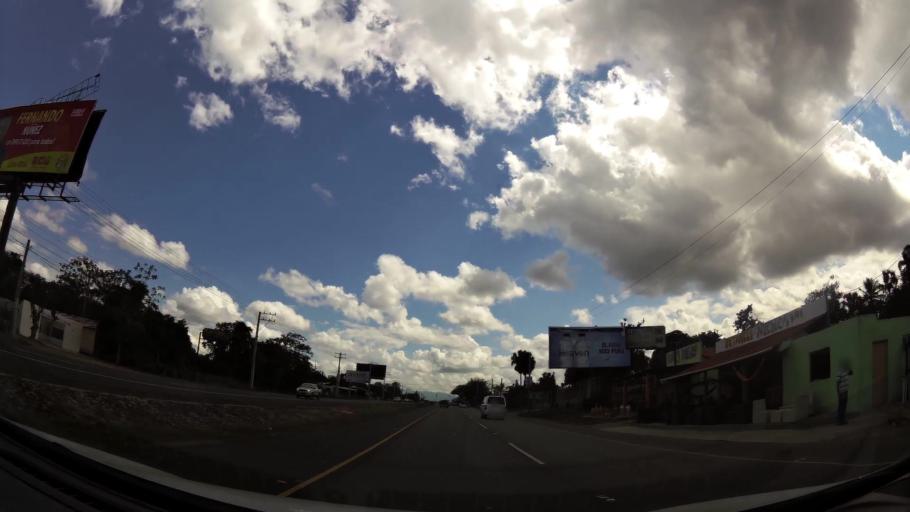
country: DO
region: La Vega
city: Rio Verde Arriba
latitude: 19.3503
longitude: -70.6005
